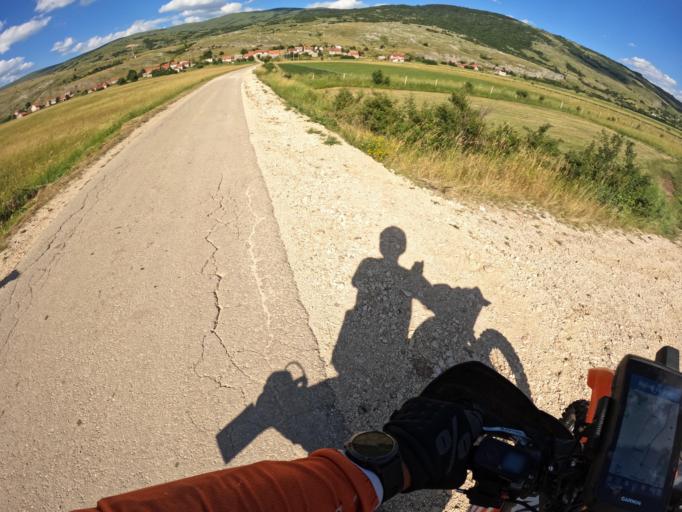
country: BA
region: Federation of Bosnia and Herzegovina
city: Glamoc
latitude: 43.9897
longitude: 16.9180
